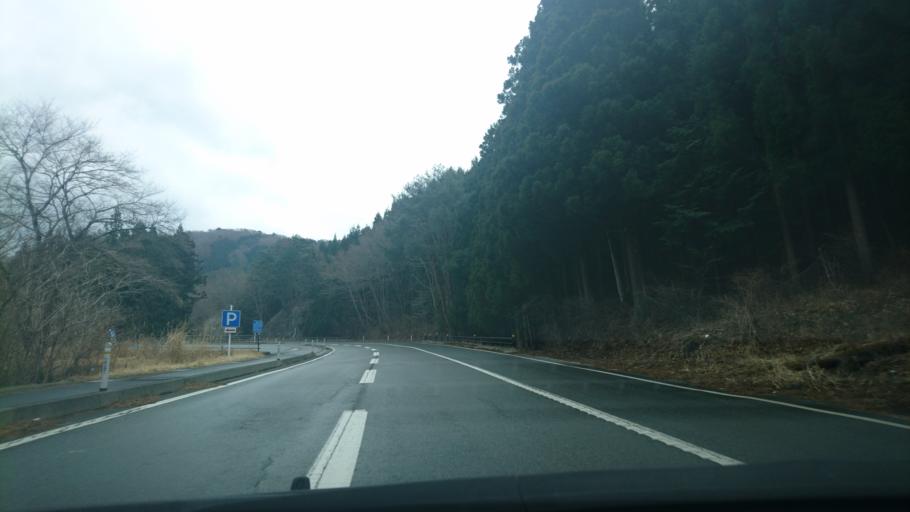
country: JP
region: Iwate
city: Ofunato
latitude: 39.1366
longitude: 141.8202
